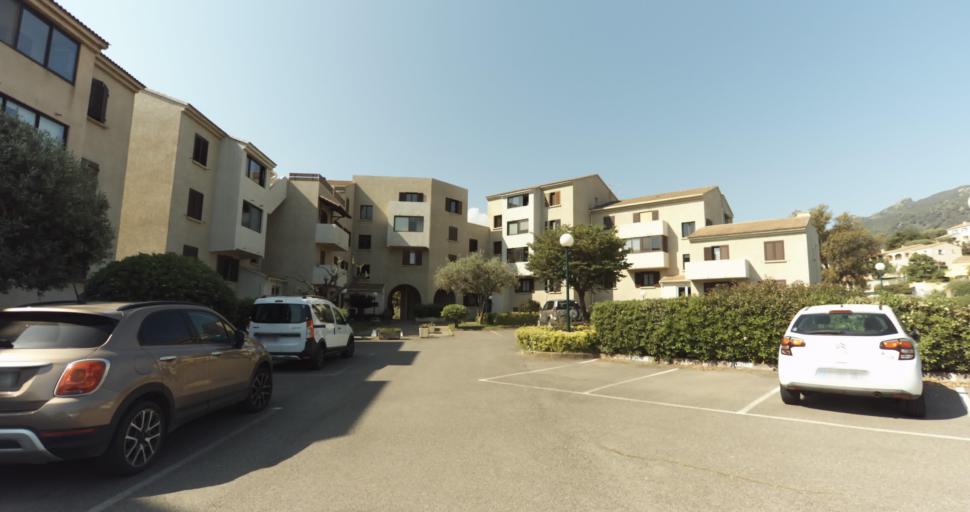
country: FR
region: Corsica
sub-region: Departement de la Haute-Corse
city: Biguglia
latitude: 42.6236
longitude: 9.4337
